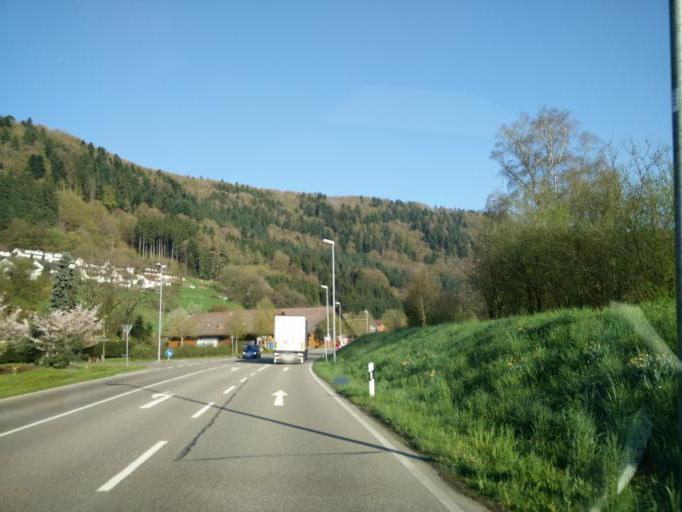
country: DE
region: Baden-Wuerttemberg
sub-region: Karlsruhe Region
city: Calw
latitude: 48.7402
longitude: 8.7335
